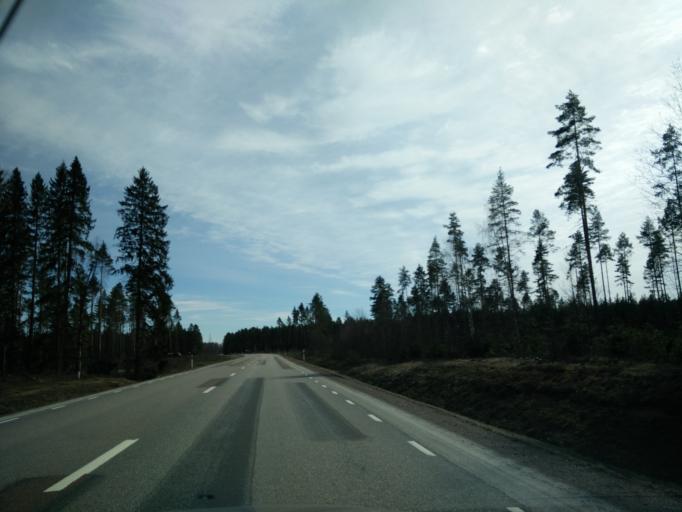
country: SE
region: Vaermland
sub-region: Hagfors Kommun
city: Hagfors
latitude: 60.0179
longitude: 13.5931
